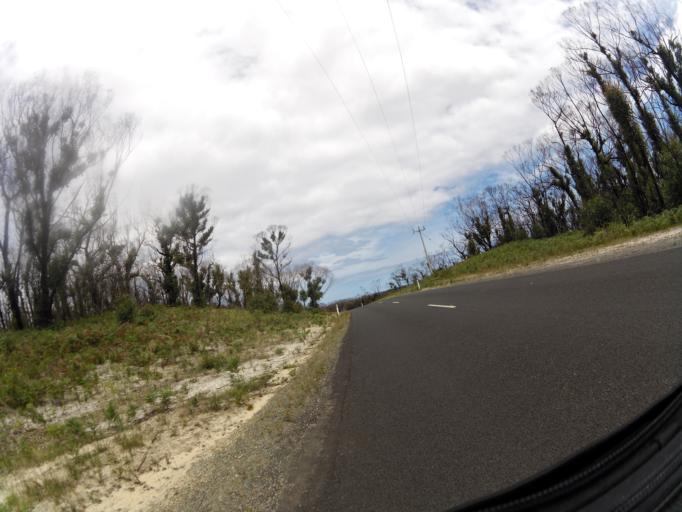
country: AU
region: Victoria
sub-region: East Gippsland
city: Lakes Entrance
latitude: -37.7939
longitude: 148.7309
